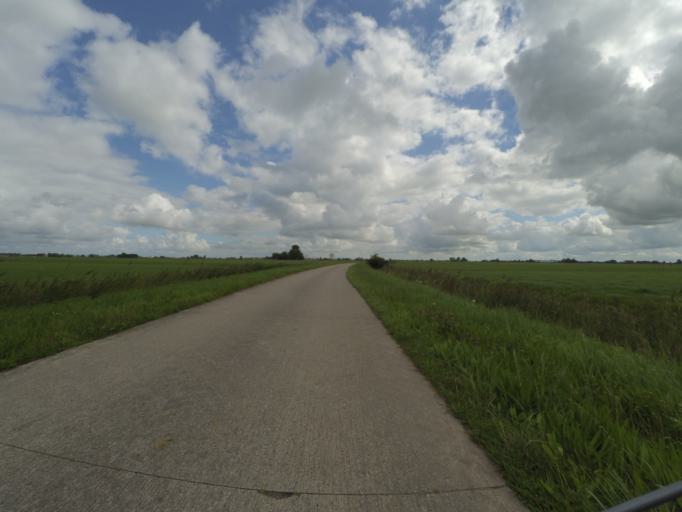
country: NL
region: Friesland
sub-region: Gemeente Kollumerland en Nieuwkruisland
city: Kollum
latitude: 53.2735
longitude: 6.1937
